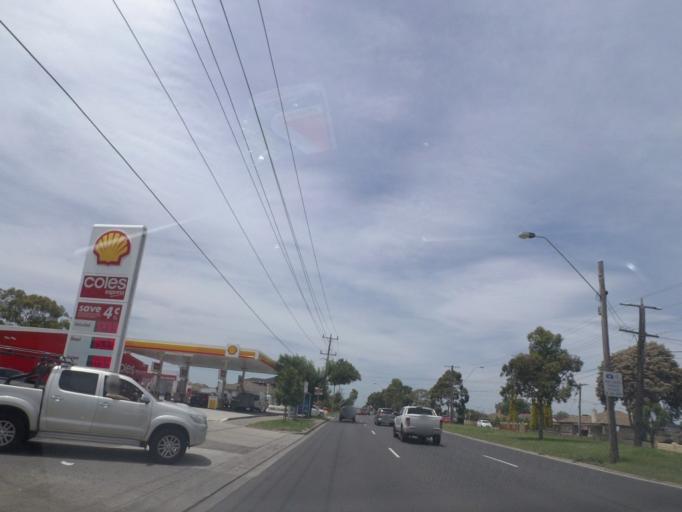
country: AU
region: Victoria
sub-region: Maribyrnong
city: Braybrook
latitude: -37.7785
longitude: 144.8432
